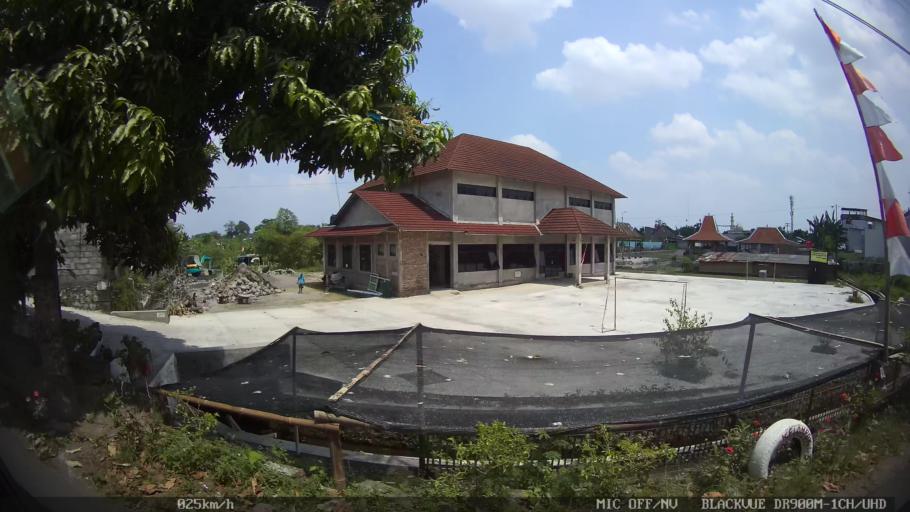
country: ID
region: Daerah Istimewa Yogyakarta
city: Yogyakarta
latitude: -7.8222
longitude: 110.4052
